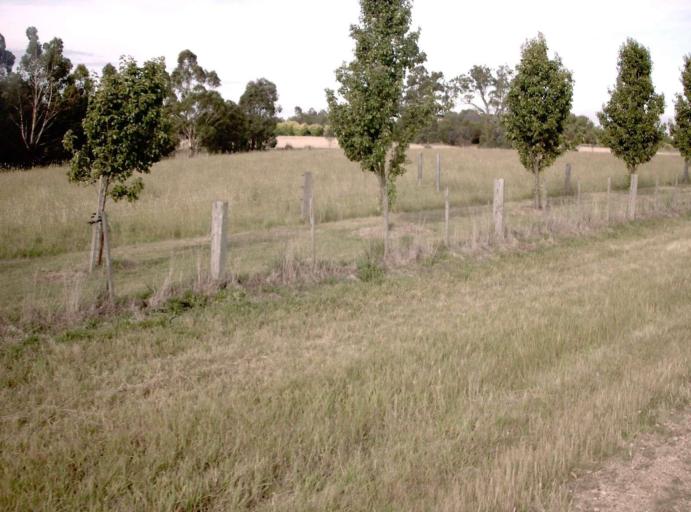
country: AU
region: Victoria
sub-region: Wellington
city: Heyfield
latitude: -38.0179
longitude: 146.7164
